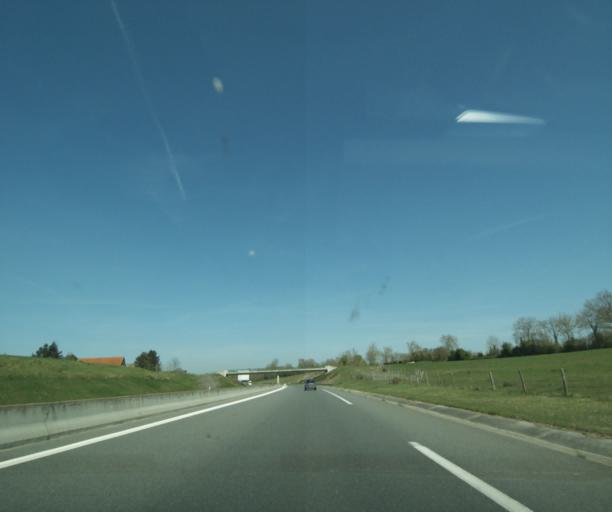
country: FR
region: Auvergne
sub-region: Departement de l'Allier
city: Trevol
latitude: 46.6183
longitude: 3.2897
